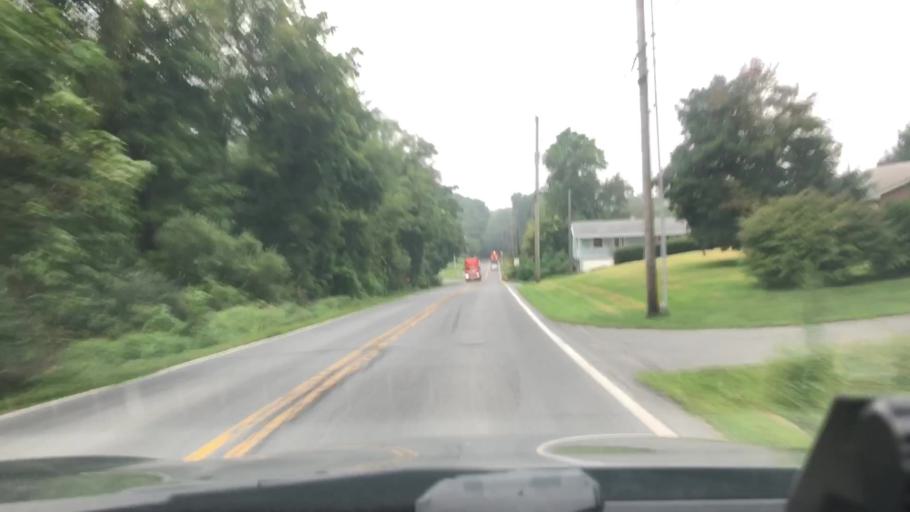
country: US
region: Pennsylvania
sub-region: Berks County
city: Kutztown
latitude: 40.5702
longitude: -75.8070
